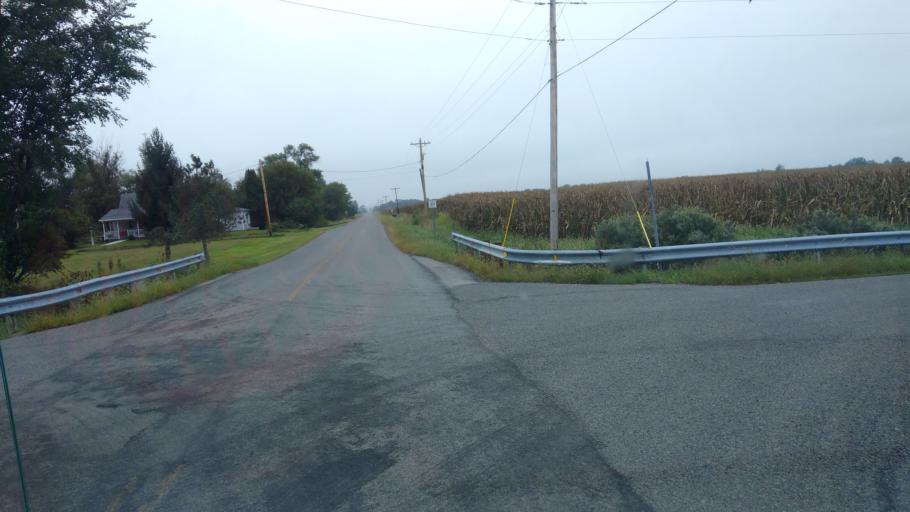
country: US
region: Ohio
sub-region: Logan County
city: Northwood
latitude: 40.4521
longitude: -83.5662
